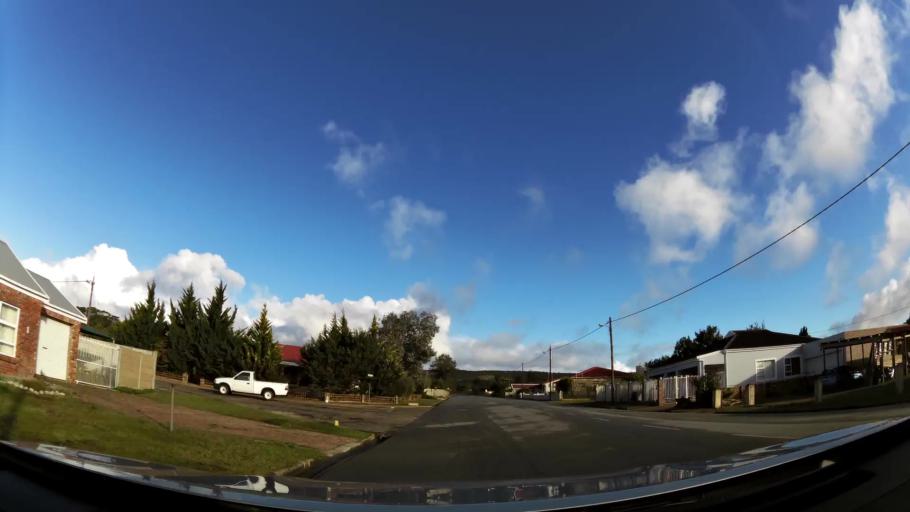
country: ZA
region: Western Cape
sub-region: Eden District Municipality
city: Riversdale
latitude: -34.2073
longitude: 21.5864
